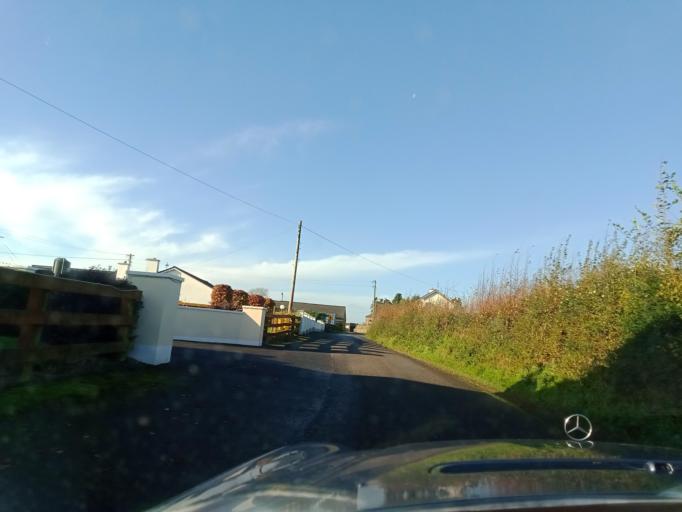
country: IE
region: Leinster
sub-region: Kilkenny
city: Mooncoin
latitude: 52.3002
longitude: -7.2166
